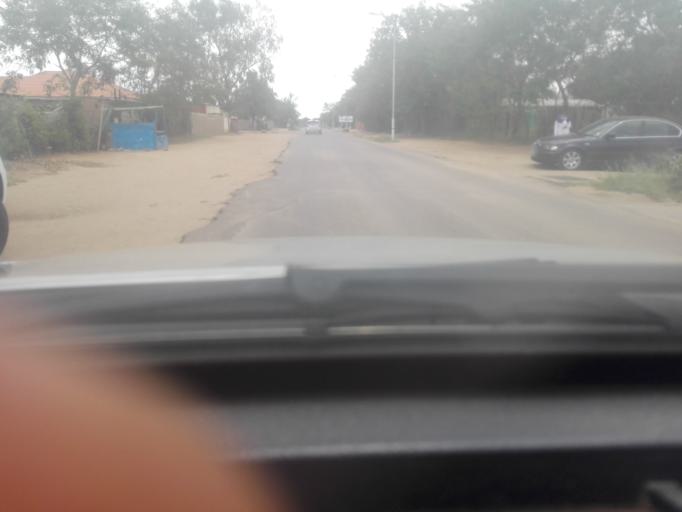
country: BW
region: South East
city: Gaborone
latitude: -24.6222
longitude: 25.9408
